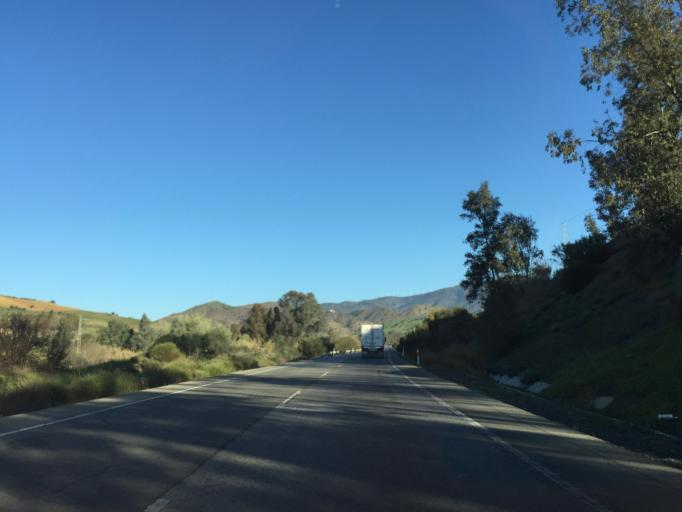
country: ES
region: Andalusia
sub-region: Provincia de Malaga
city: Pizarra
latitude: 36.7918
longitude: -4.7509
